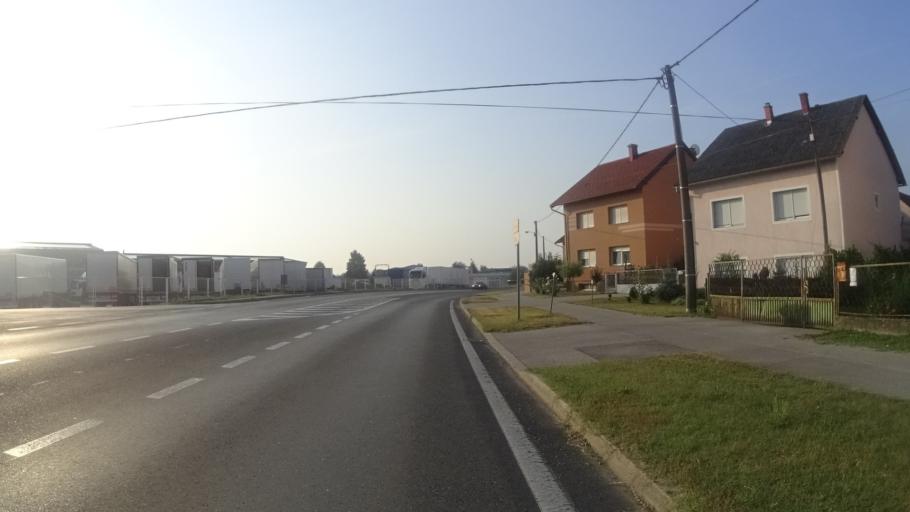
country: HR
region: Varazdinska
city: Petrijanec
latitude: 46.3393
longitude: 16.2494
